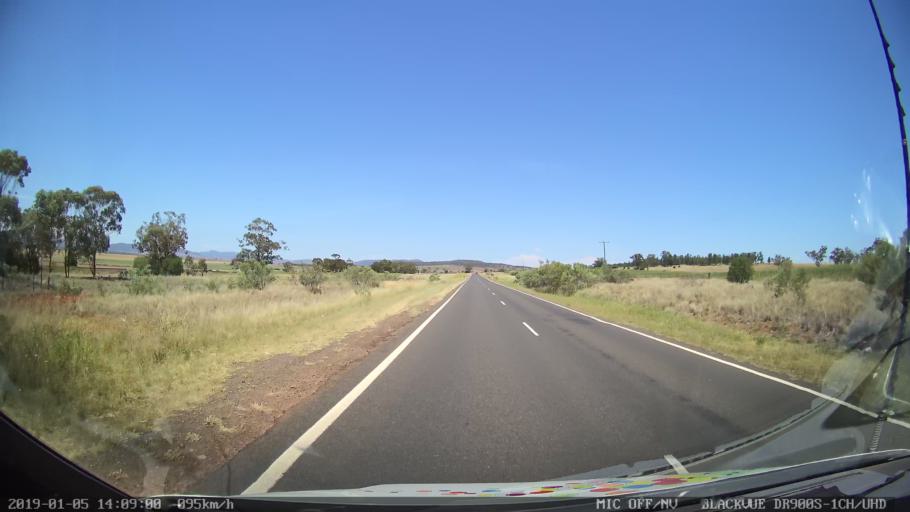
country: AU
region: New South Wales
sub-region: Gunnedah
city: Gunnedah
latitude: -31.2396
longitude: 150.4208
